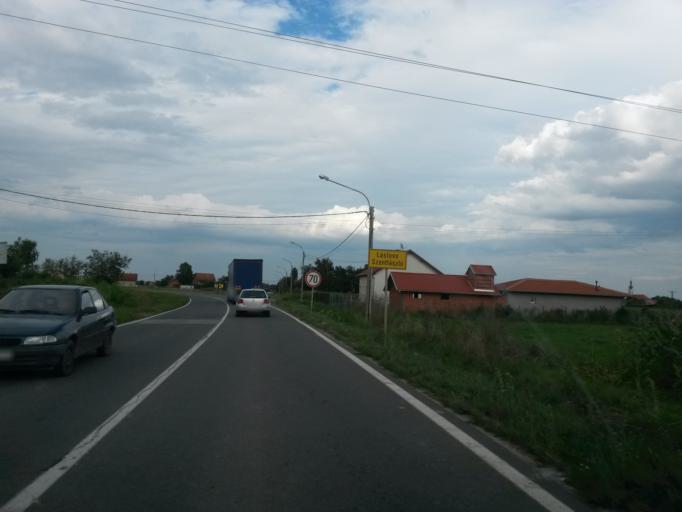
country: HR
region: Osjecko-Baranjska
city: Laslovo
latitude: 45.4154
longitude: 18.6872
